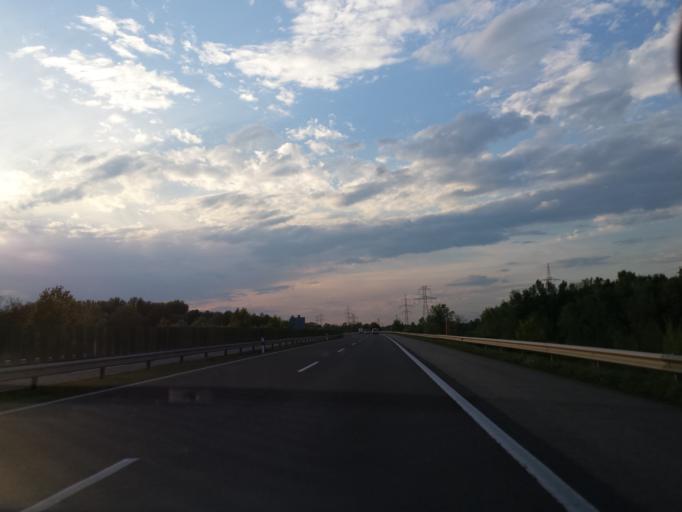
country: HU
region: Gyor-Moson-Sopron
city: Abda
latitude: 47.6835
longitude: 17.5398
